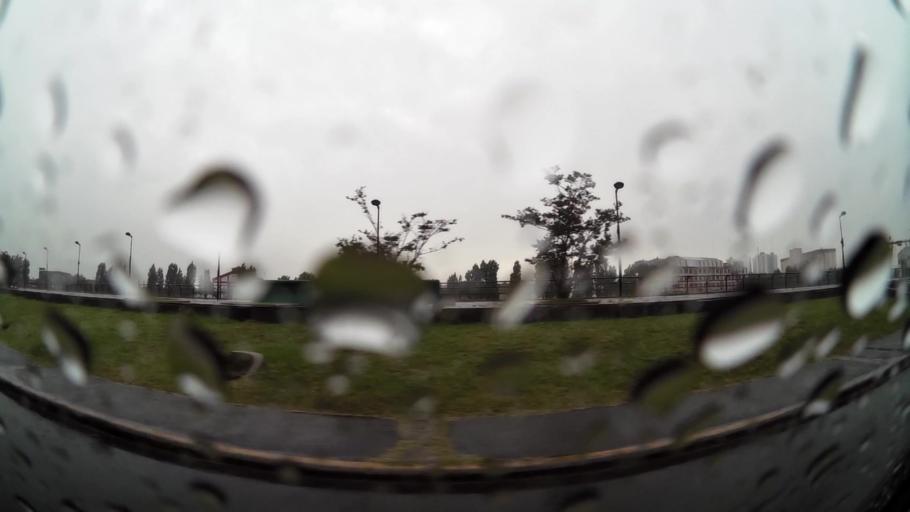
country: AR
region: Buenos Aires
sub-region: Partido de Avellaneda
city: Avellaneda
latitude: -34.6479
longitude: -58.3640
